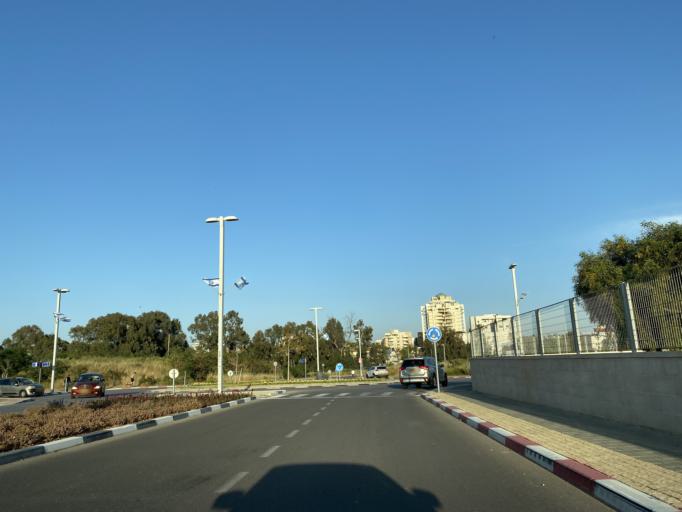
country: IL
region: Tel Aviv
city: Herzliyya
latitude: 32.1600
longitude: 34.8336
